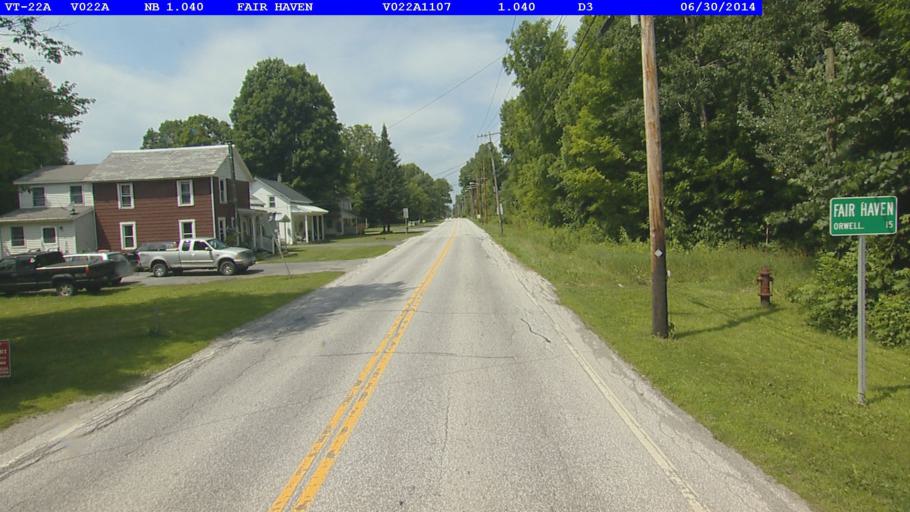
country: US
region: Vermont
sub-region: Rutland County
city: Fair Haven
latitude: 43.5831
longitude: -73.2648
